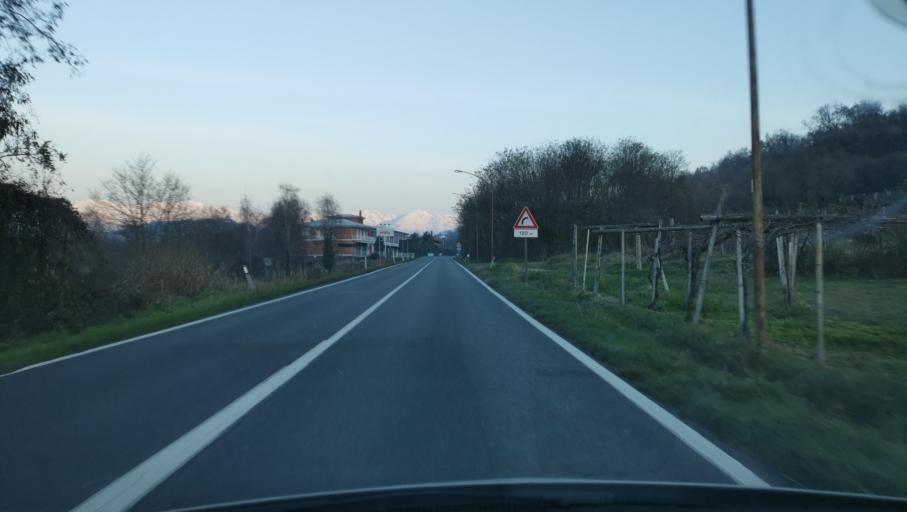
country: IT
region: Piedmont
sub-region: Provincia di Torino
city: Barone Canavese
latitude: 45.3158
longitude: 7.8800
